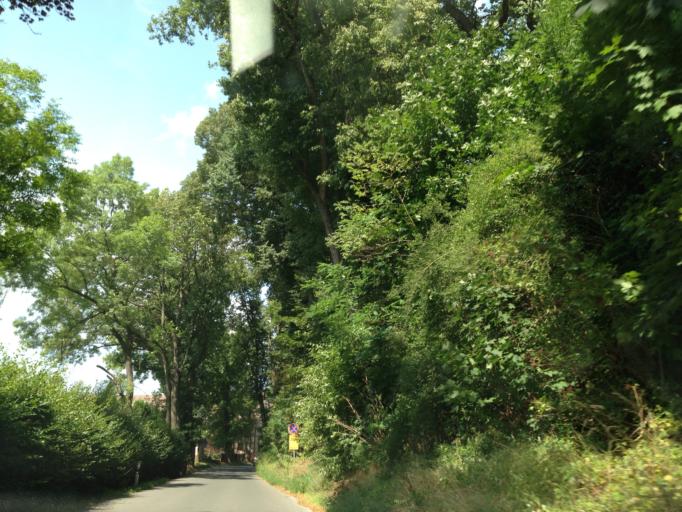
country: DE
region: Thuringia
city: Herschdorf
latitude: 50.7226
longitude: 11.5398
